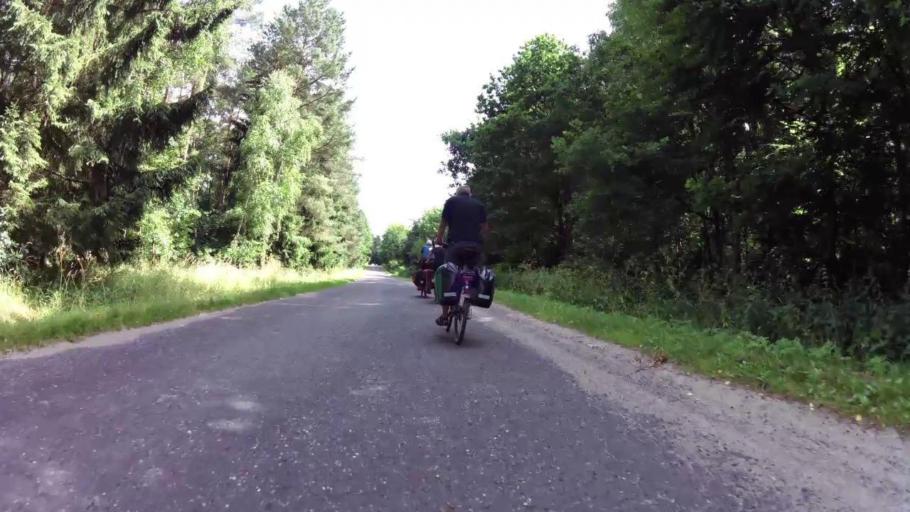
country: PL
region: West Pomeranian Voivodeship
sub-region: Powiat lobeski
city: Lobez
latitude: 53.6638
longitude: 15.5529
